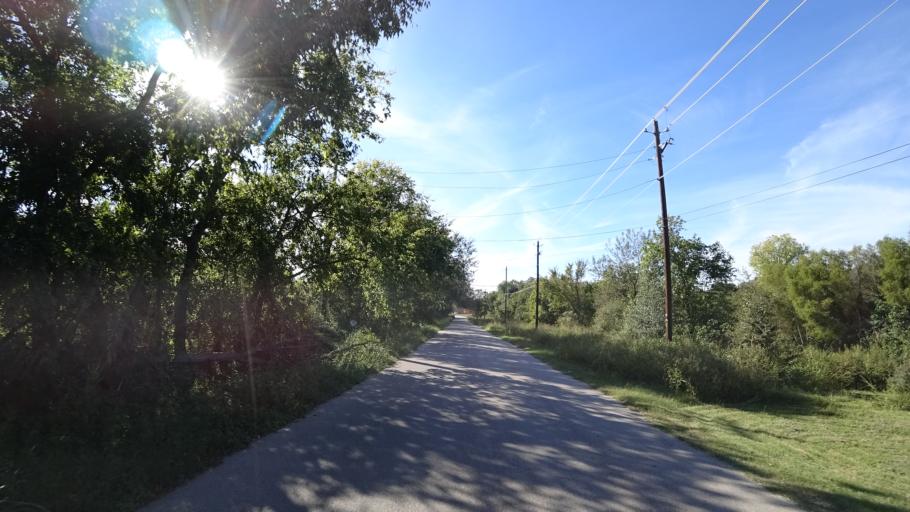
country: US
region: Texas
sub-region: Travis County
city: Austin
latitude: 30.2620
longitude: -97.6697
